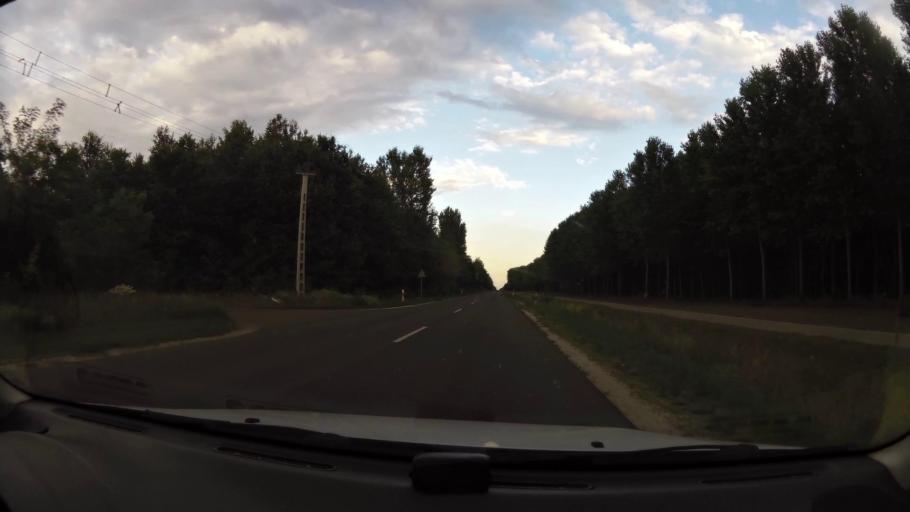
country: HU
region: Pest
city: Ujszilvas
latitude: 47.2917
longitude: 19.9035
